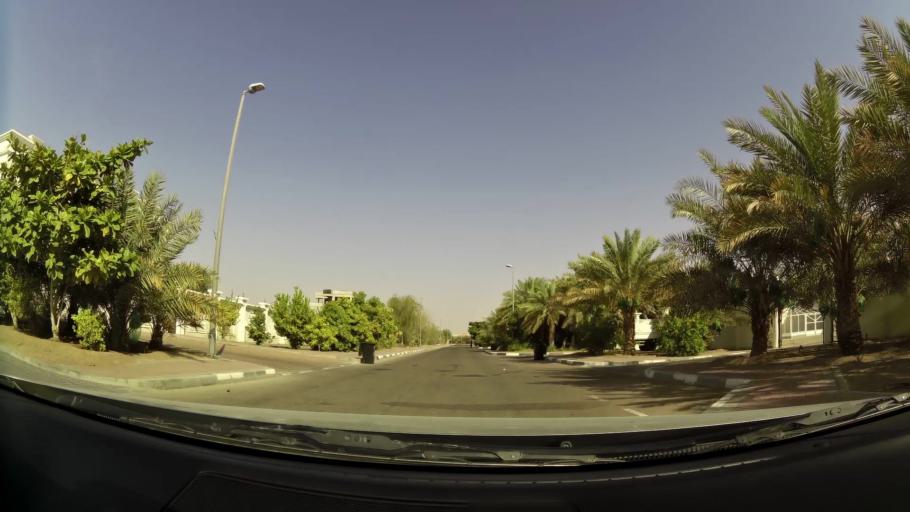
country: OM
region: Al Buraimi
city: Al Buraymi
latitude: 24.3428
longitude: 55.8004
